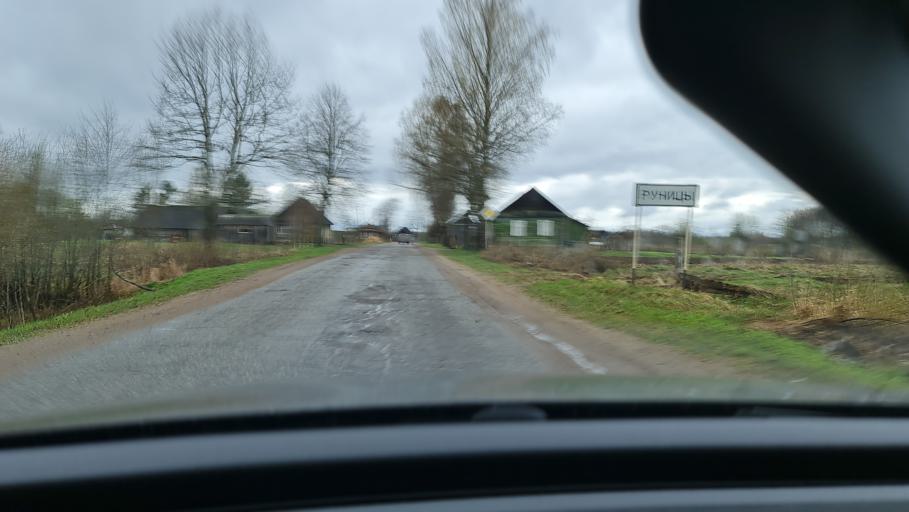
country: RU
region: Novgorod
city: Marevo
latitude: 57.2425
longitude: 32.0494
